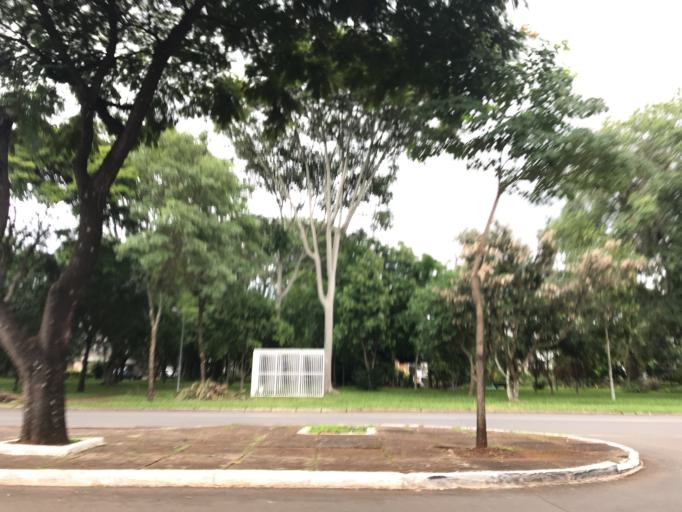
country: BR
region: Federal District
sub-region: Brasilia
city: Brasilia
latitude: -15.8248
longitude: -47.9232
